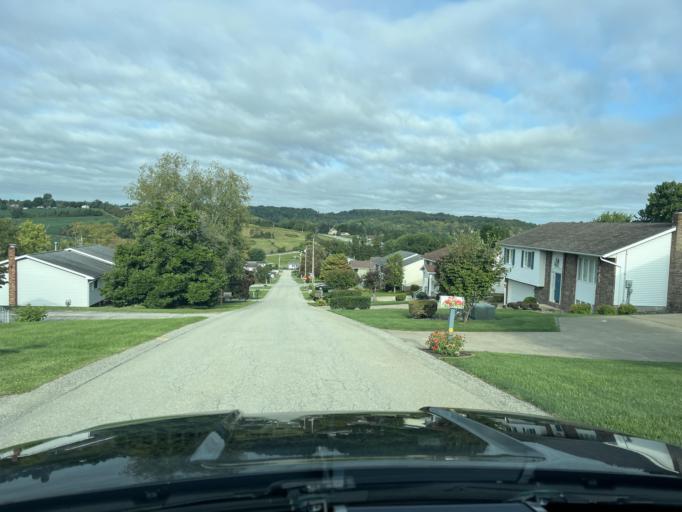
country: US
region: Pennsylvania
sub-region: Fayette County
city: Leith-Hatfield
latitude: 39.8793
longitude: -79.7398
